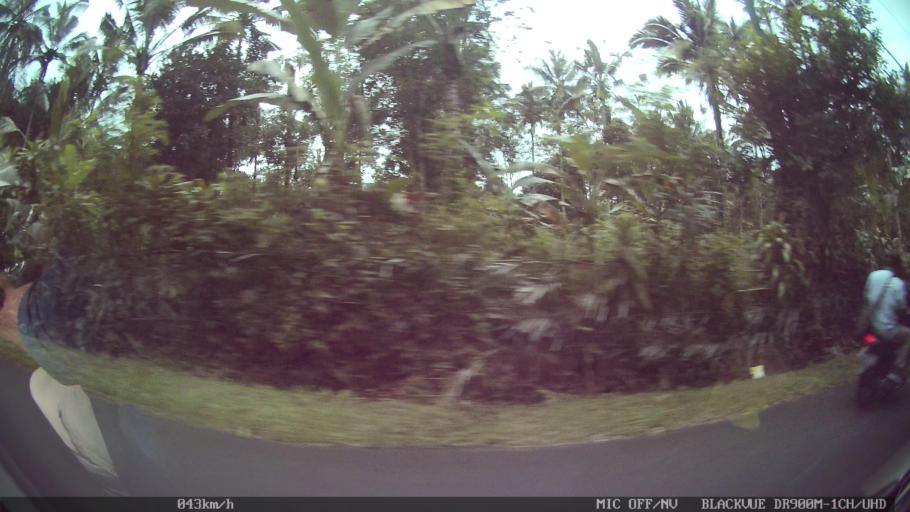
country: ID
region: Bali
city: Banjar Geriana Kangin
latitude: -8.3951
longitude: 115.4420
